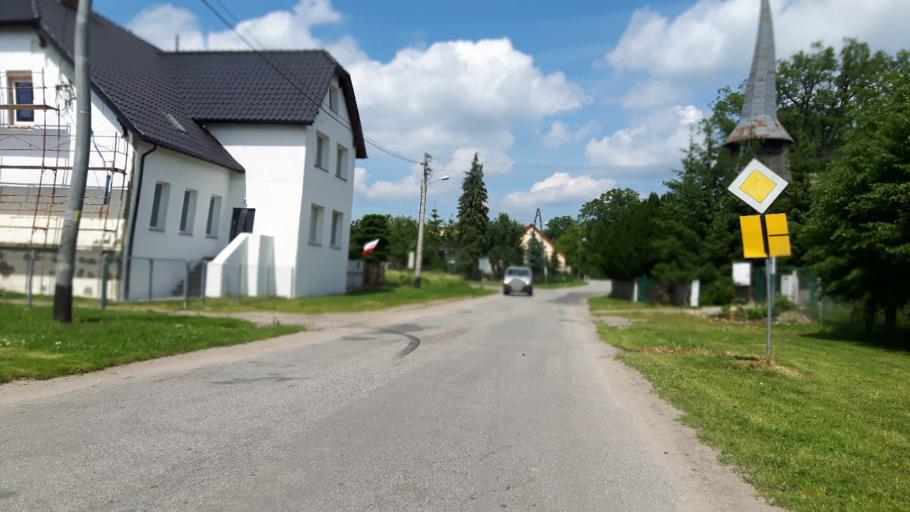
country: PL
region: West Pomeranian Voivodeship
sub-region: Powiat goleniowski
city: Osina
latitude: 53.6597
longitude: 14.9769
